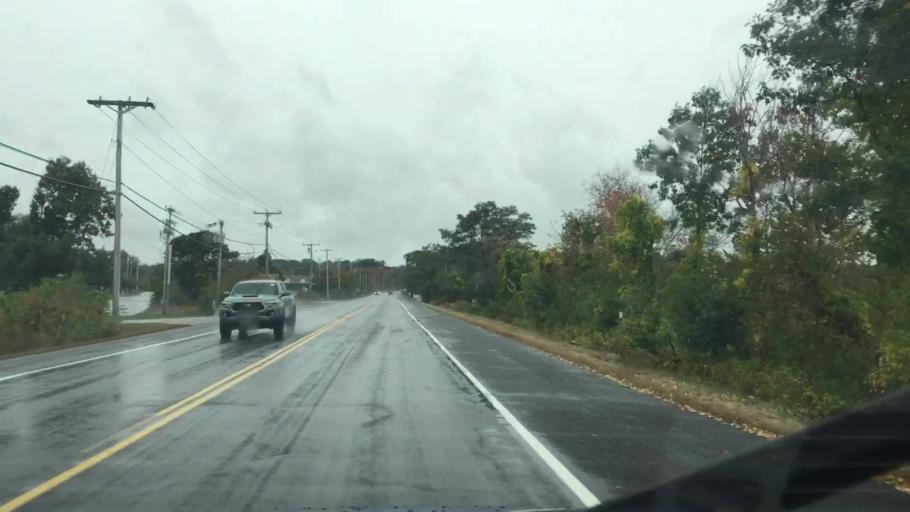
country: US
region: Massachusetts
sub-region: Essex County
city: Salisbury
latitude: 42.8701
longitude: -70.8336
